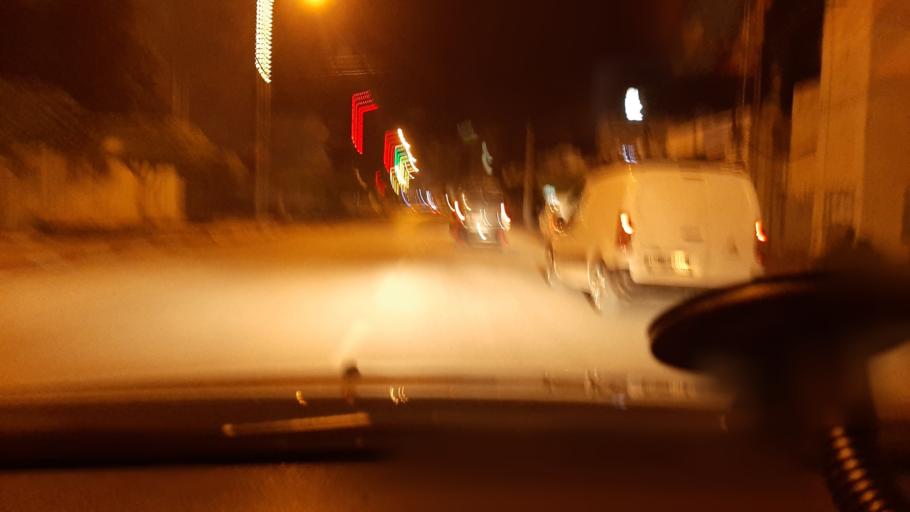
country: TN
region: Safaqis
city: Sfax
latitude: 34.7831
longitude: 10.7225
